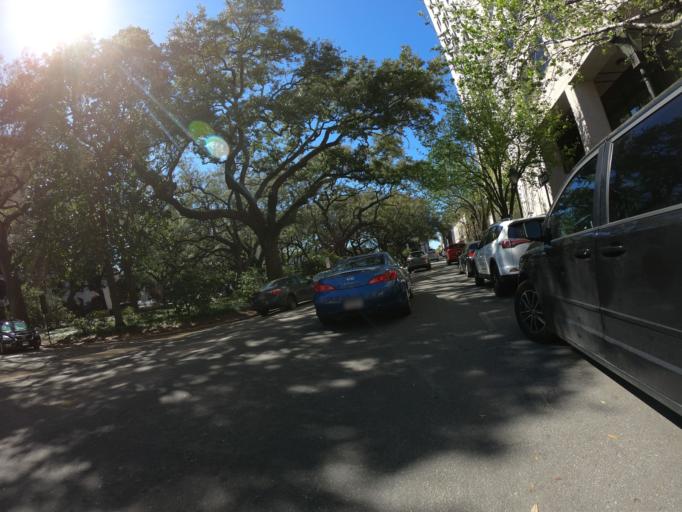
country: US
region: Georgia
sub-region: Chatham County
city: Savannah
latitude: 32.0801
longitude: -81.0909
